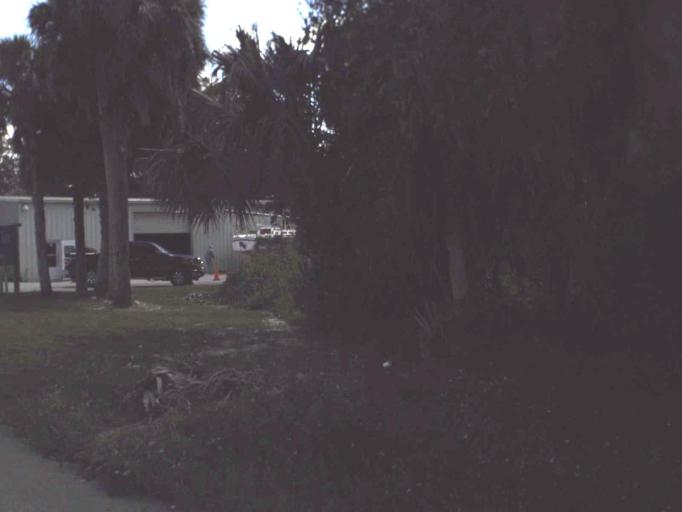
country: US
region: Florida
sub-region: Okeechobee County
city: Taylor Creek
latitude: 27.2095
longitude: -80.7903
